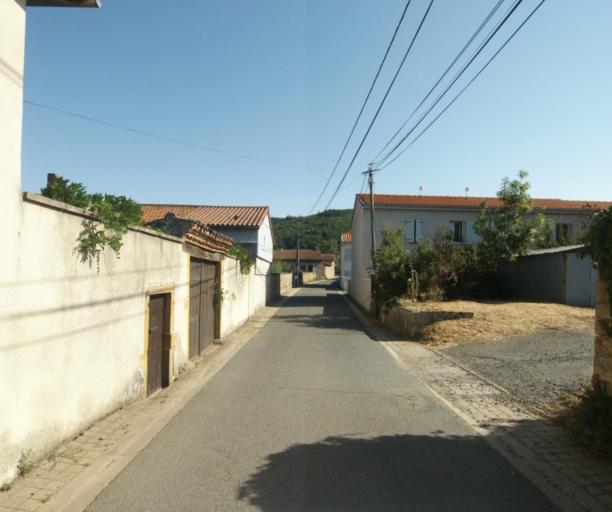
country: FR
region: Rhone-Alpes
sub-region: Departement du Rhone
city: Saint-Pierre-la-Palud
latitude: 45.7725
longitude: 4.6078
